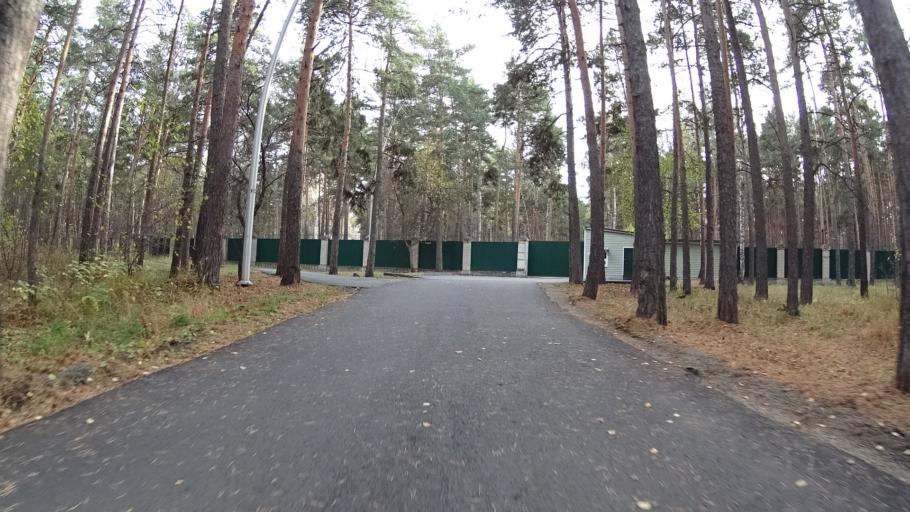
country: RU
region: Chelyabinsk
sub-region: Gorod Chelyabinsk
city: Chelyabinsk
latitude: 55.1378
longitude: 61.3512
